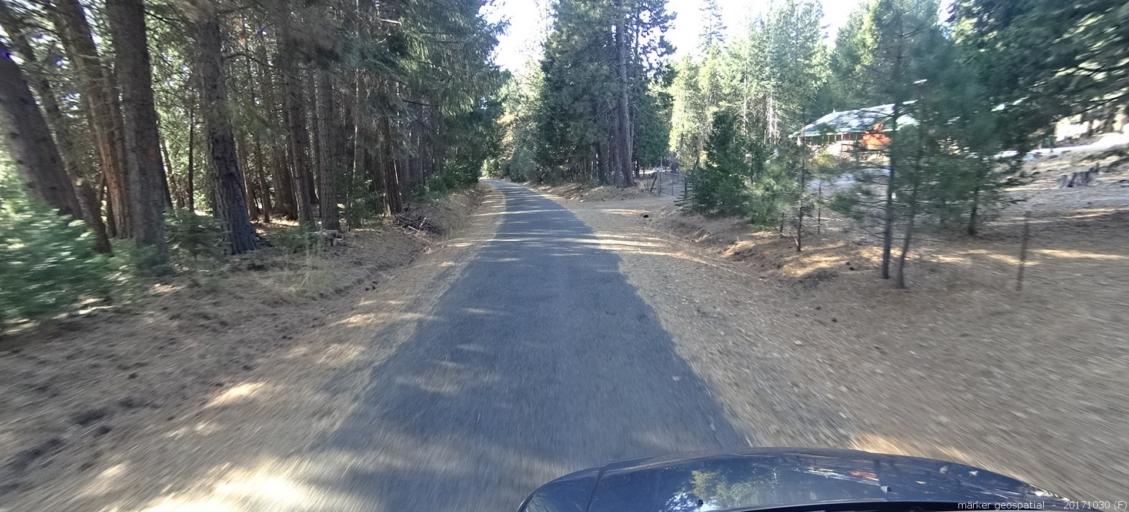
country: US
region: California
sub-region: Shasta County
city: Shingletown
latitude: 40.5317
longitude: -121.7036
